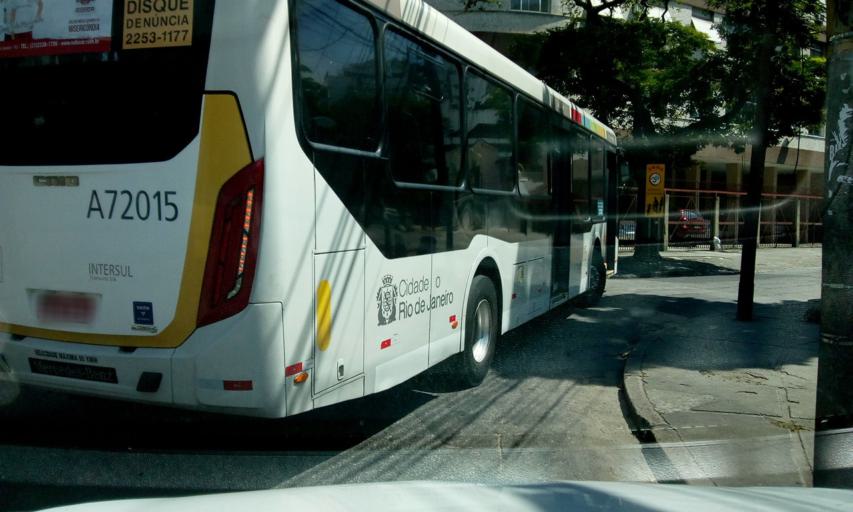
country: BR
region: Rio de Janeiro
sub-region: Rio De Janeiro
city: Rio de Janeiro
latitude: -22.9179
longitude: -43.2632
